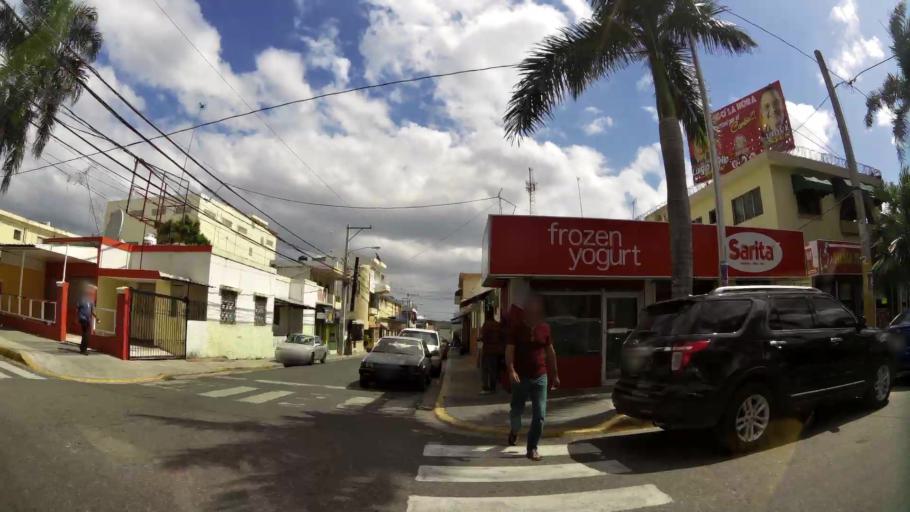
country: DO
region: San Cristobal
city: San Cristobal
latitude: 18.4181
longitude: -70.1121
